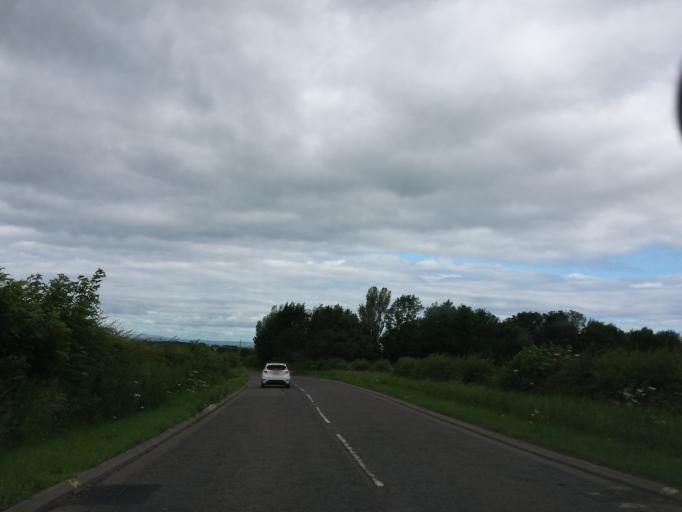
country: GB
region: Scotland
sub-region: East Lothian
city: Gullane
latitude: 55.9894
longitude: -2.8300
